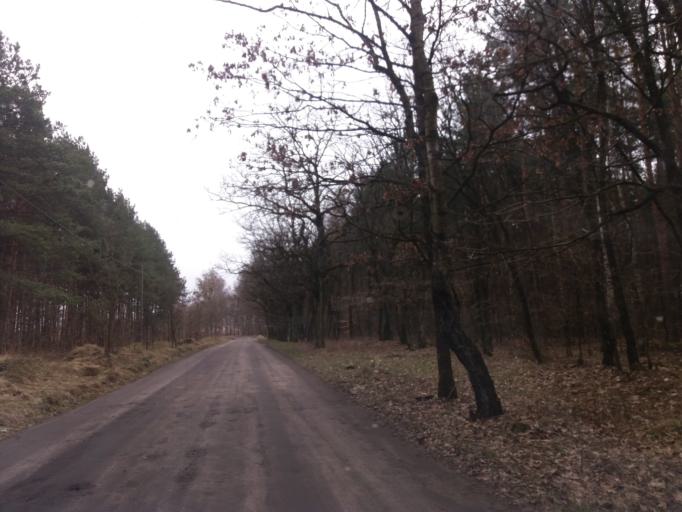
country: PL
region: West Pomeranian Voivodeship
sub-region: Powiat choszczenski
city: Drawno
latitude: 53.2144
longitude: 15.7330
